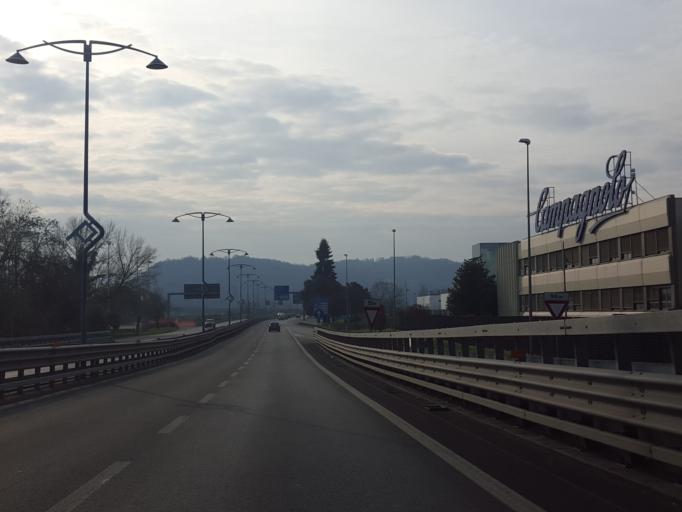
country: IT
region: Veneto
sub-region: Provincia di Vicenza
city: Creazzo
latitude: 45.5247
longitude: 11.5075
